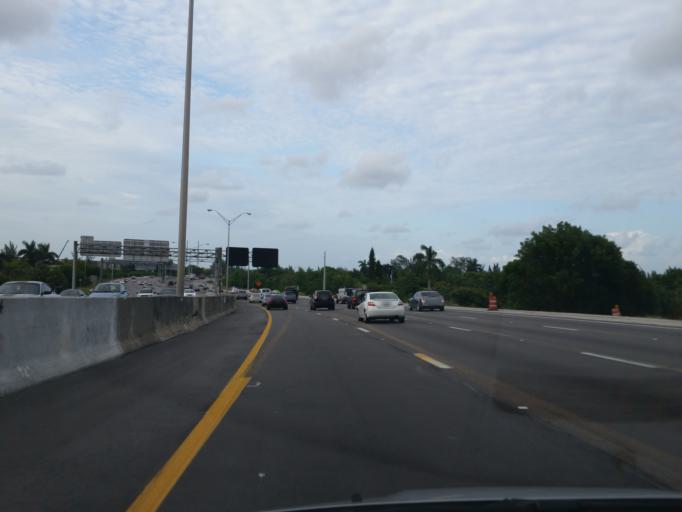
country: US
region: Florida
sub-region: Miami-Dade County
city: Ives Estates
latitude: 25.9430
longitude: -80.1879
